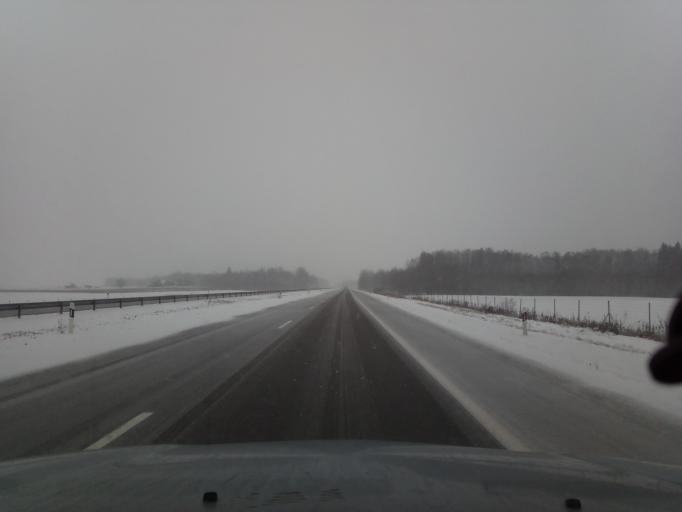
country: LT
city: Sirvintos
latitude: 55.0484
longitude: 24.8937
